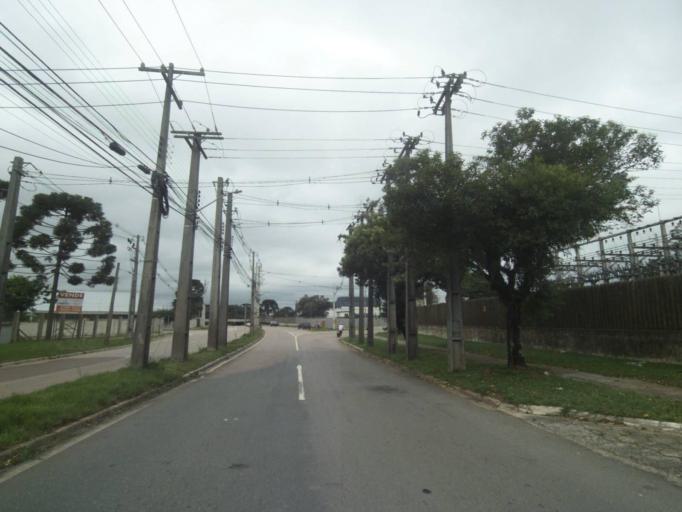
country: BR
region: Parana
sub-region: Sao Jose Dos Pinhais
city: Sao Jose dos Pinhais
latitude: -25.5541
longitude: -49.3084
